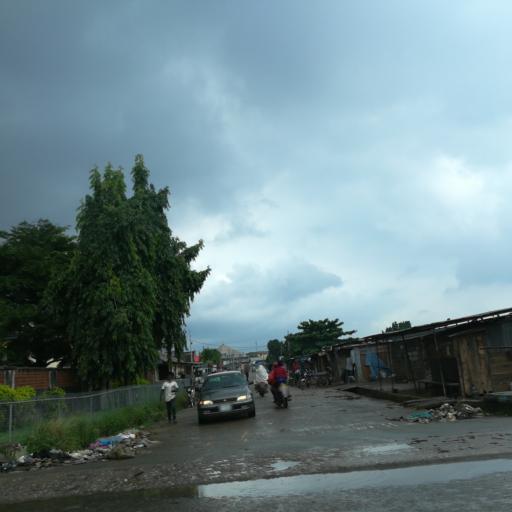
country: NG
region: Lagos
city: Agege
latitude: 6.5948
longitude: 3.2935
